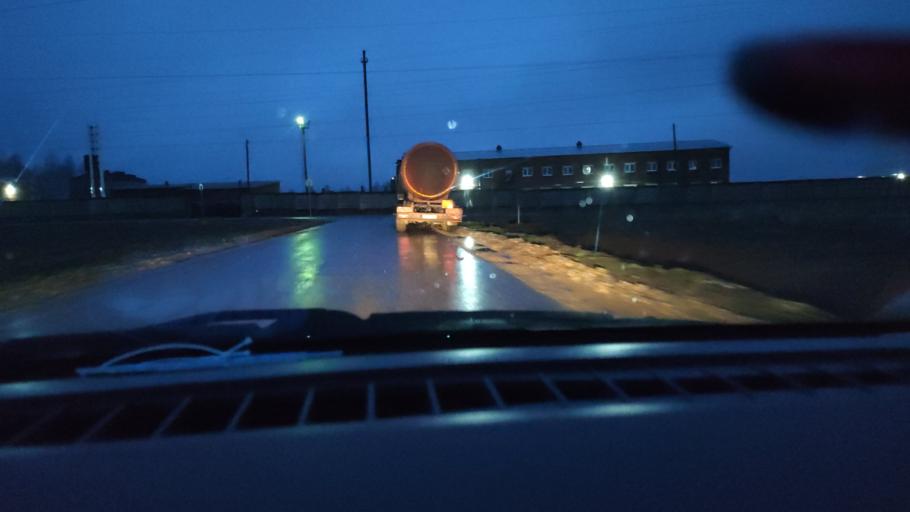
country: RU
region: Udmurtiya
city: Mozhga
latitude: 56.4361
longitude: 52.2501
